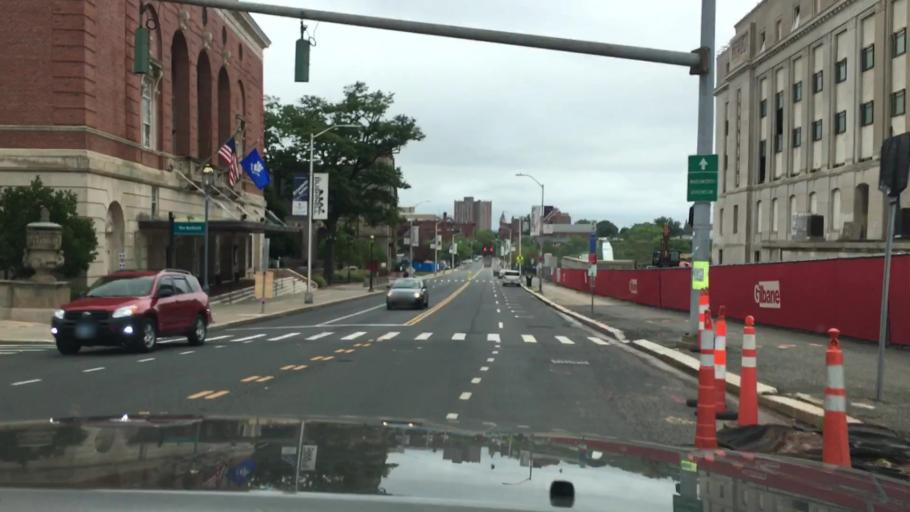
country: US
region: Connecticut
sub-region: Hartford County
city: Hartford
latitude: 41.7625
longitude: -72.6814
